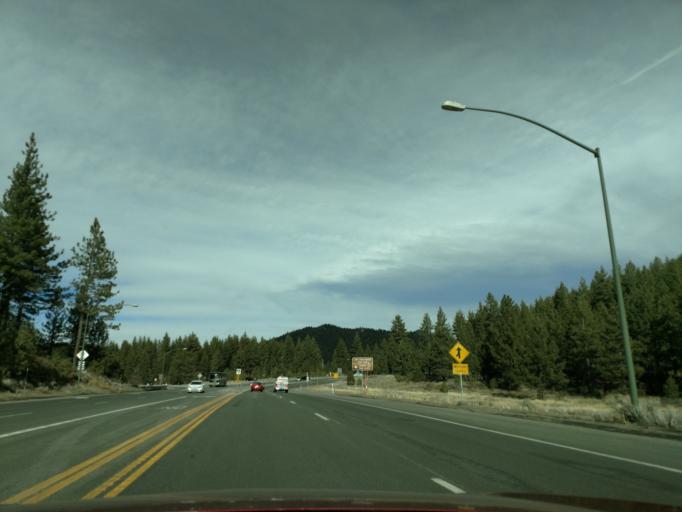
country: US
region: Nevada
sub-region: Douglas County
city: Kingsbury
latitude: 39.0984
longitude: -119.9103
